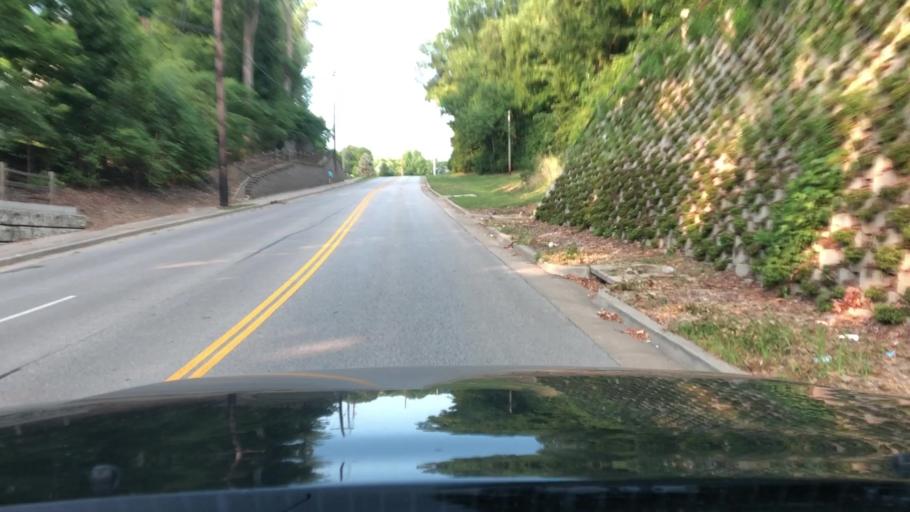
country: US
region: Missouri
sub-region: Saint Charles County
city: Saint Charles
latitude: 38.8090
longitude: -90.5390
